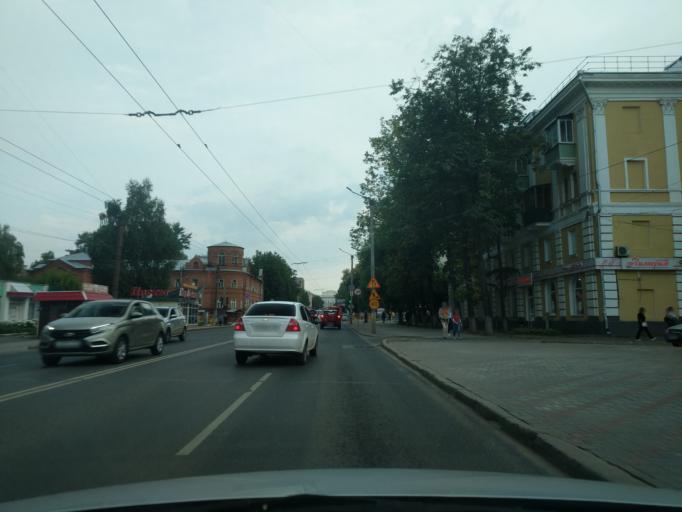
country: RU
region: Kirov
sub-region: Kirovo-Chepetskiy Rayon
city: Kirov
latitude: 58.6124
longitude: 49.6672
